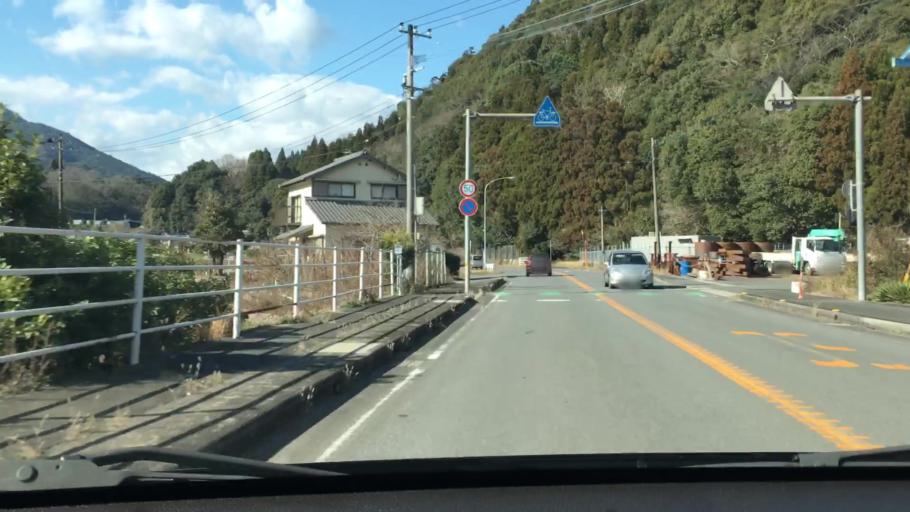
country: JP
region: Oita
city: Saiki
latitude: 32.9883
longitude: 131.8369
